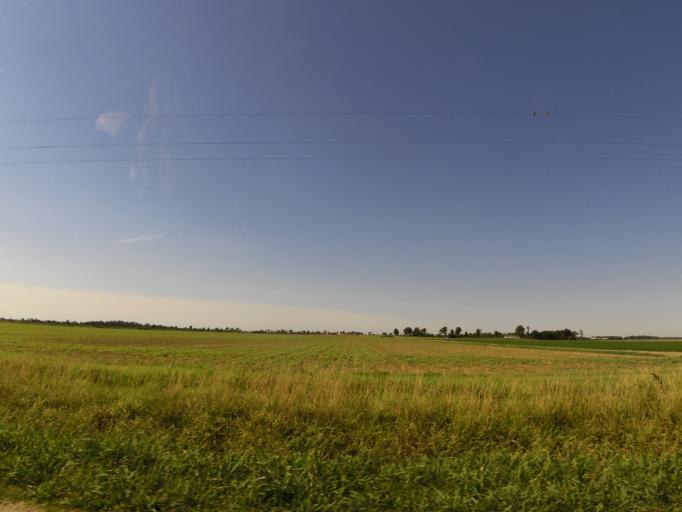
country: US
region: Arkansas
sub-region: Clay County
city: Corning
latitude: 36.4352
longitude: -90.4648
